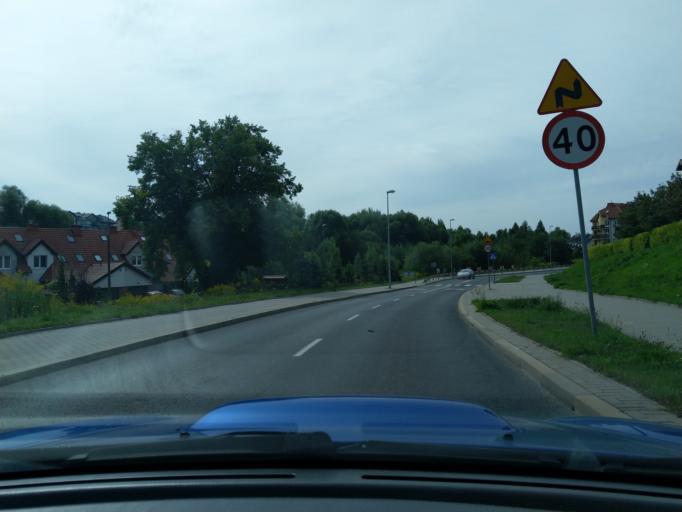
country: PL
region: Warmian-Masurian Voivodeship
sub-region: Olsztyn
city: Kortowo
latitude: 53.7386
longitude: 20.4828
